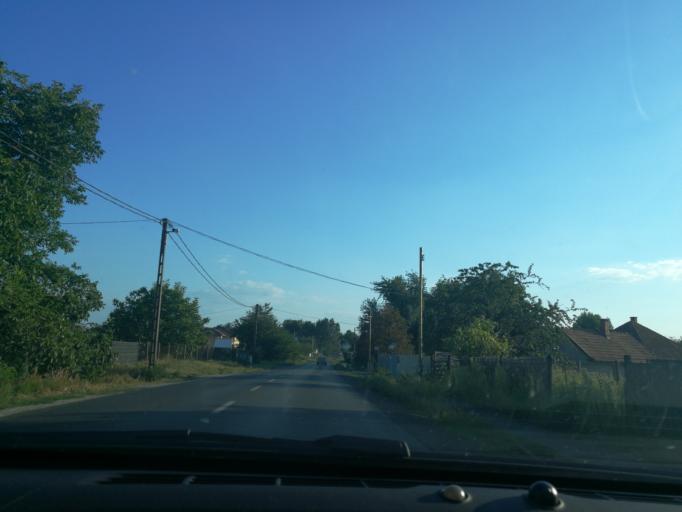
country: HU
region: Szabolcs-Szatmar-Bereg
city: Kotaj
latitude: 48.0219
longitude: 21.7439
